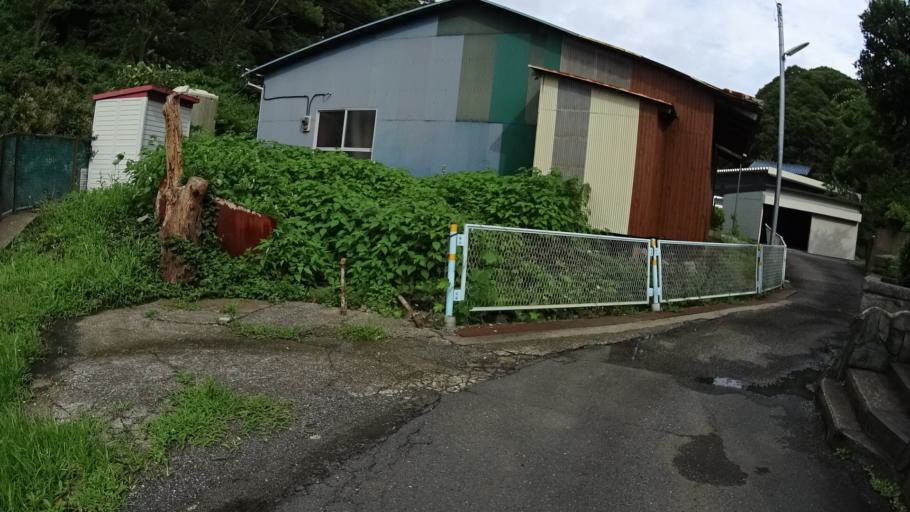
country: JP
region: Kanagawa
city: Yokosuka
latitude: 35.2760
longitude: 139.6383
